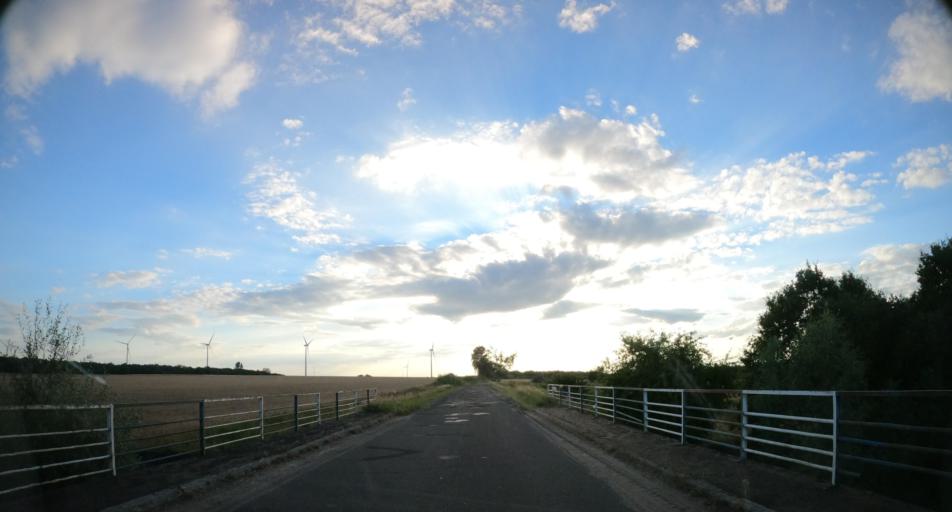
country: PL
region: West Pomeranian Voivodeship
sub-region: Powiat lobeski
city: Resko
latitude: 53.7559
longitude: 15.4431
